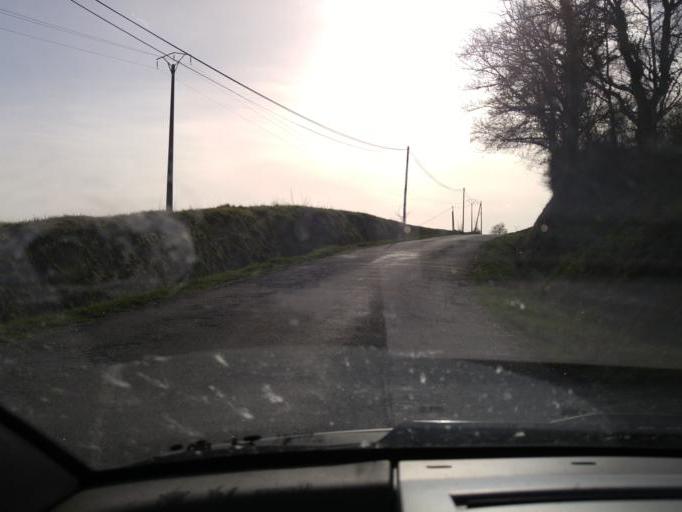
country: FR
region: Midi-Pyrenees
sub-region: Departement du Gers
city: Lectoure
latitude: 43.9344
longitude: 0.6026
